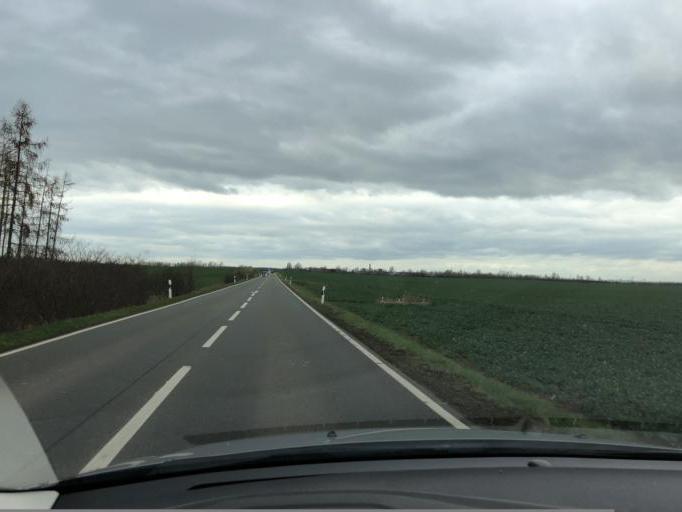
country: DE
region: Saxony-Anhalt
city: Hohenmolsen
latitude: 51.1413
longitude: 12.1389
